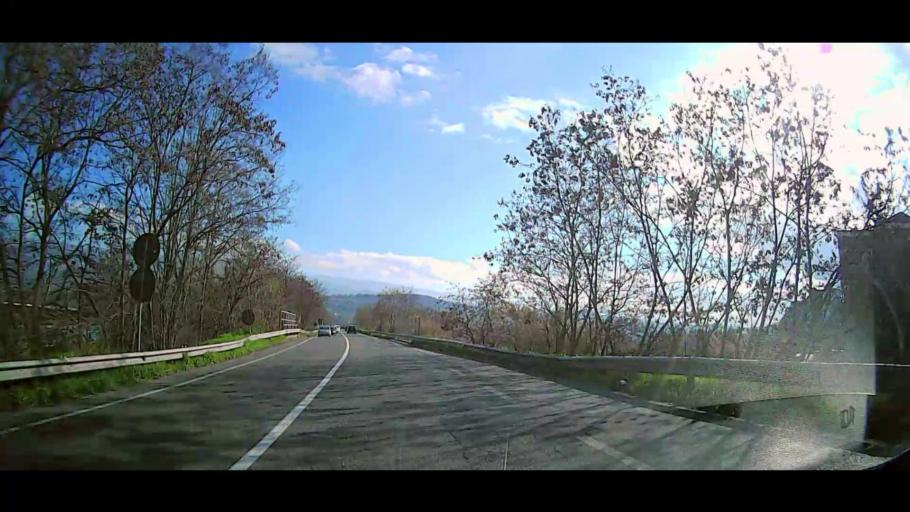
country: IT
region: Calabria
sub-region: Provincia di Cosenza
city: Quattromiglia
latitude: 39.3297
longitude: 16.2473
